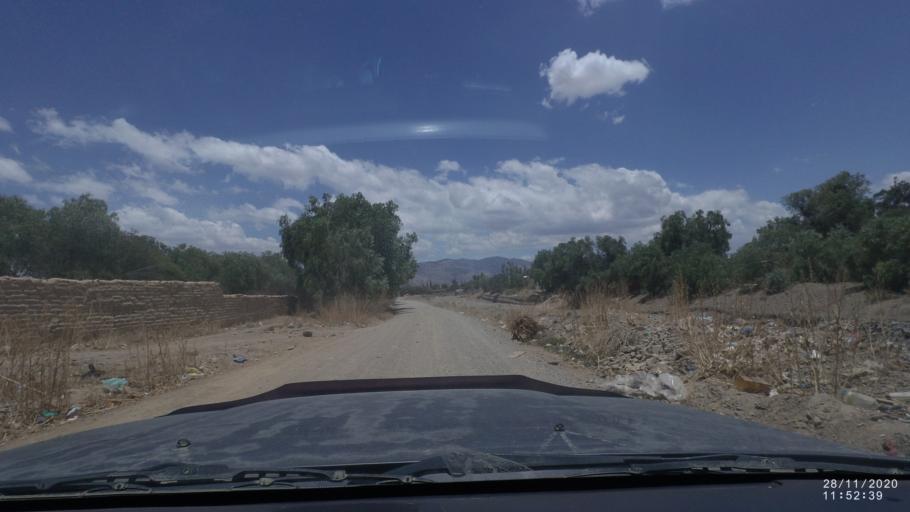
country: BO
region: Cochabamba
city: Tarata
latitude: -17.6149
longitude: -66.0217
